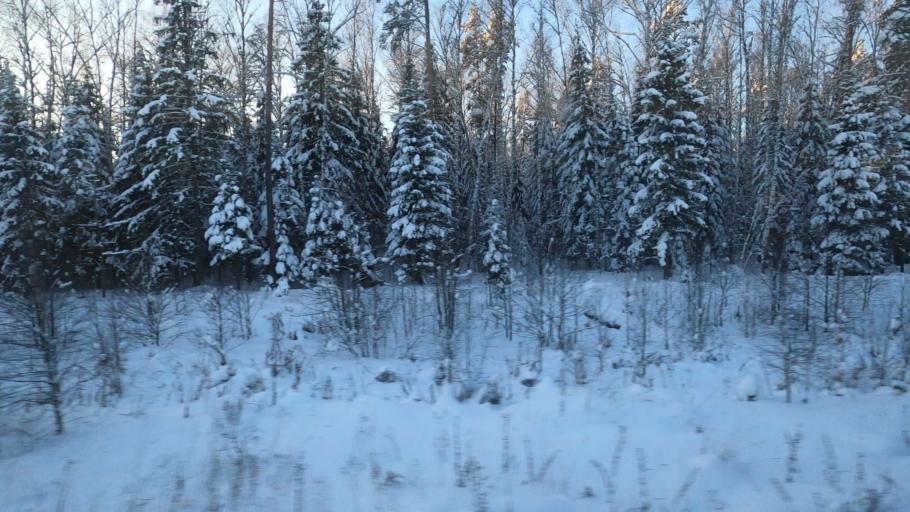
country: RU
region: Moskovskaya
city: Zhukovka
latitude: 56.5028
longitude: 37.5533
